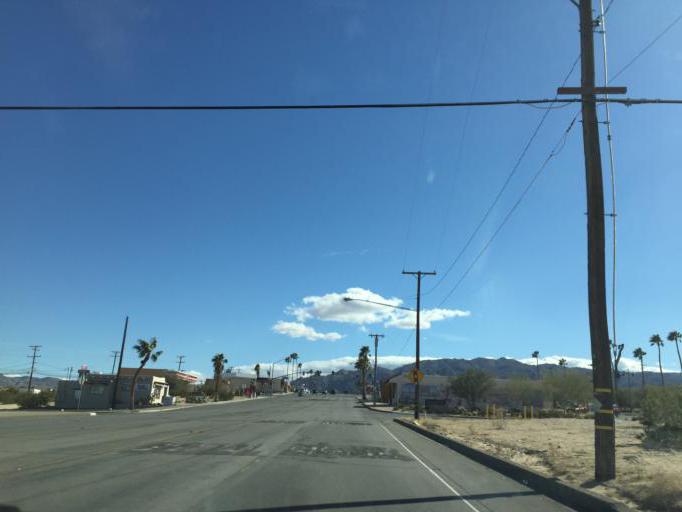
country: US
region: California
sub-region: San Bernardino County
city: Twentynine Palms
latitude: 34.1521
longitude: -116.0543
